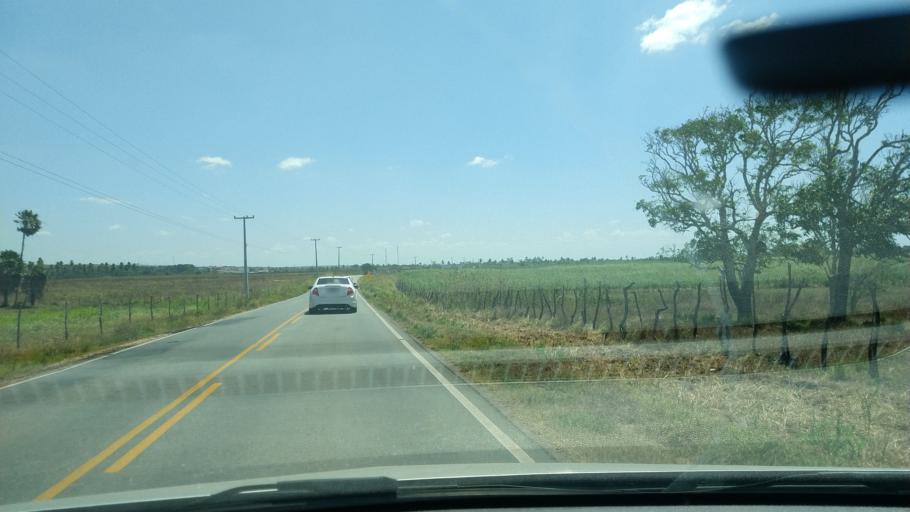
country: BR
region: Rio Grande do Norte
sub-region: Goianinha
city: Goianinha
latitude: -6.2569
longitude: -35.1947
